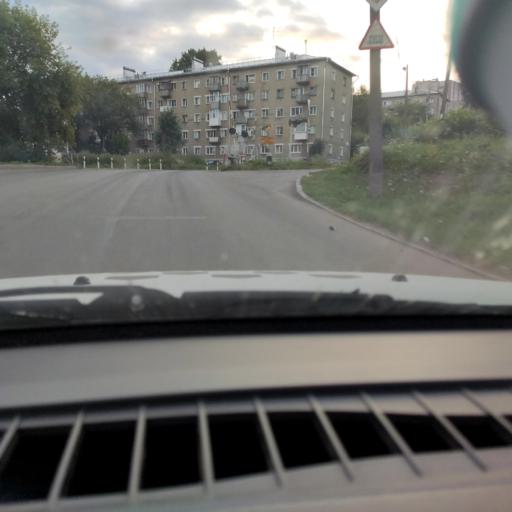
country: RU
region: Kirov
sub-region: Kirovo-Chepetskiy Rayon
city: Kirov
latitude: 58.6222
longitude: 49.6381
